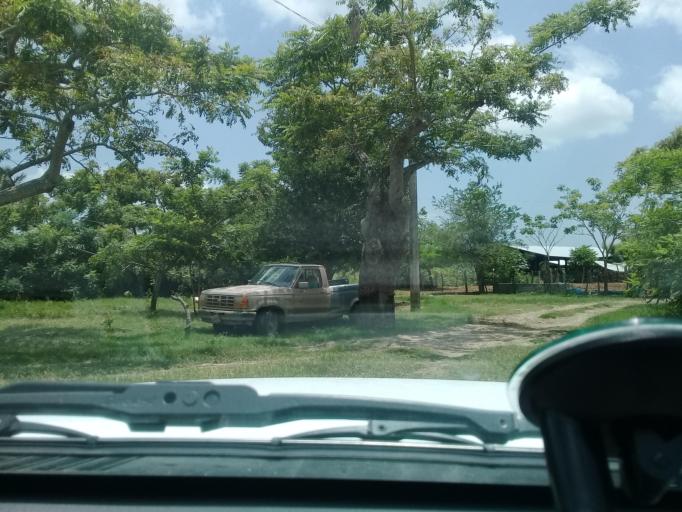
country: MX
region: Veracruz
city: Moralillo
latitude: 22.1383
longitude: -98.0401
